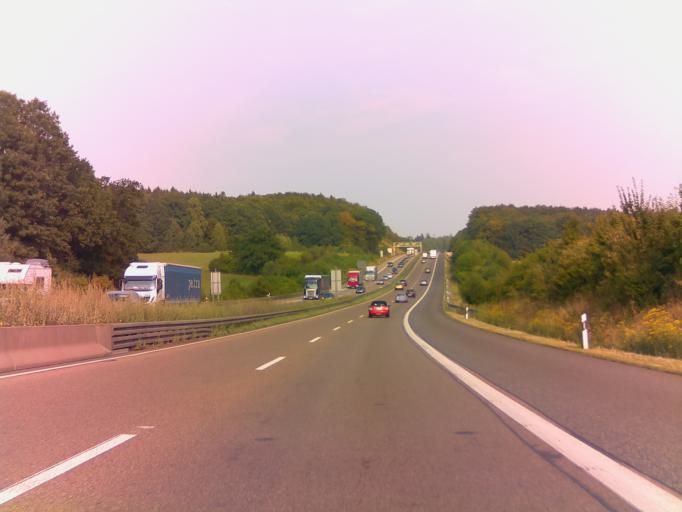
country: DE
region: Hesse
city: Kirtorf
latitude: 50.7156
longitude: 9.1177
